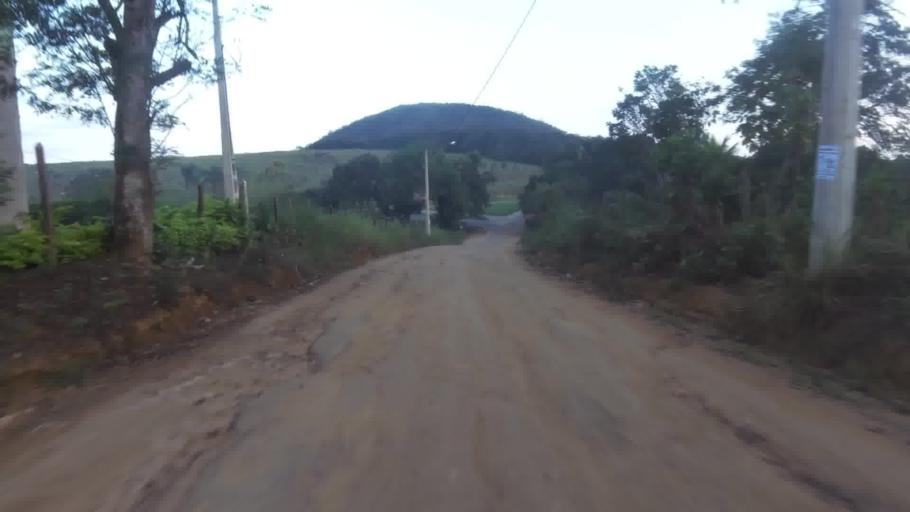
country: BR
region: Espirito Santo
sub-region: Guarapari
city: Guarapari
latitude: -20.7044
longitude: -40.5743
